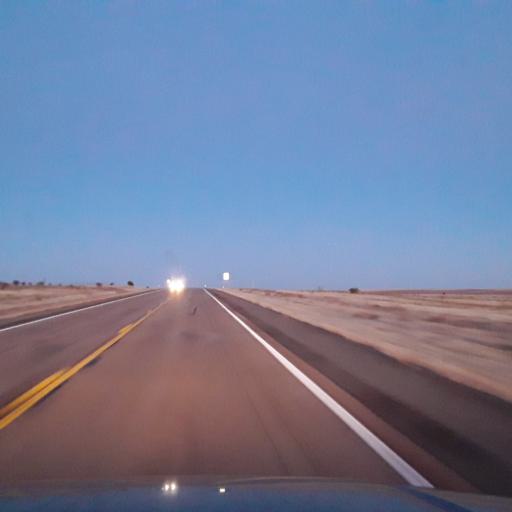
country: US
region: New Mexico
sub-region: Guadalupe County
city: Santa Rosa
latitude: 34.7682
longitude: -104.9716
